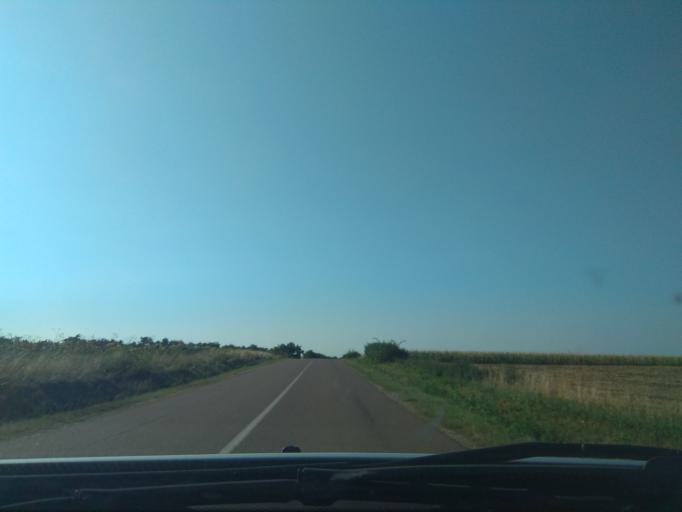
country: HU
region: Borsod-Abauj-Zemplen
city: Emod
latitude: 47.9640
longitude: 20.8018
